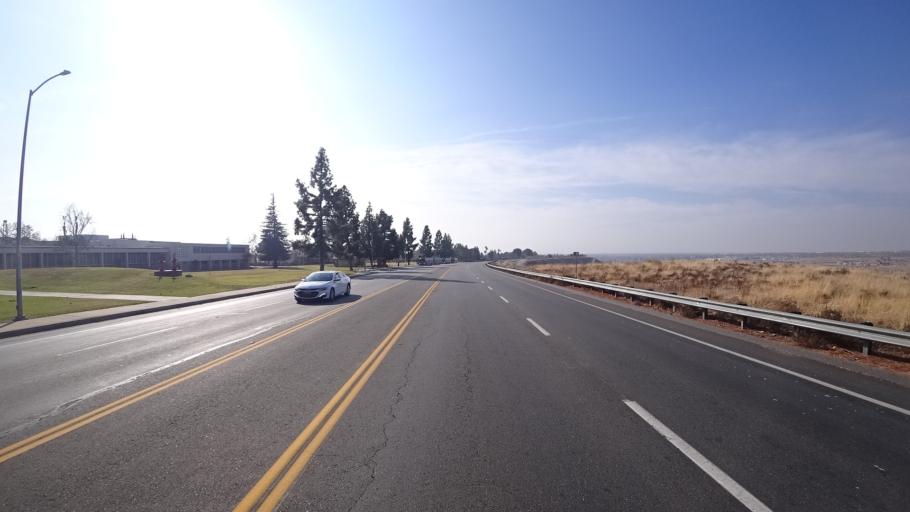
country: US
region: California
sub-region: Kern County
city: Oildale
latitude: 35.4118
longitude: -118.9713
